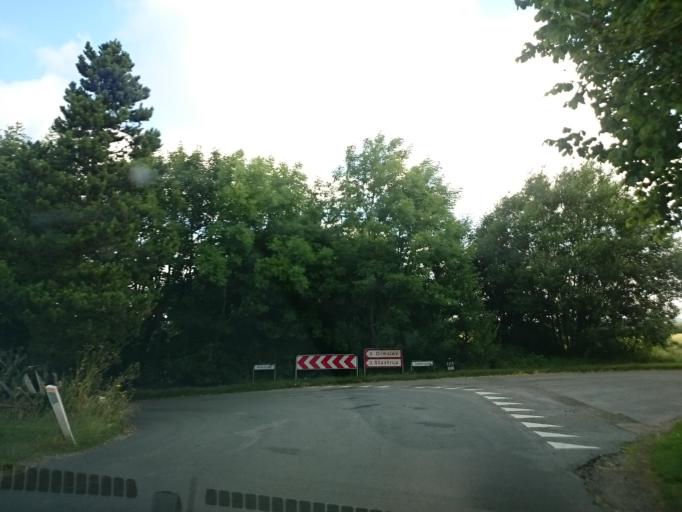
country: DK
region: Central Jutland
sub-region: Arhus Kommune
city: Stavtrup
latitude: 56.1214
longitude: 10.0979
